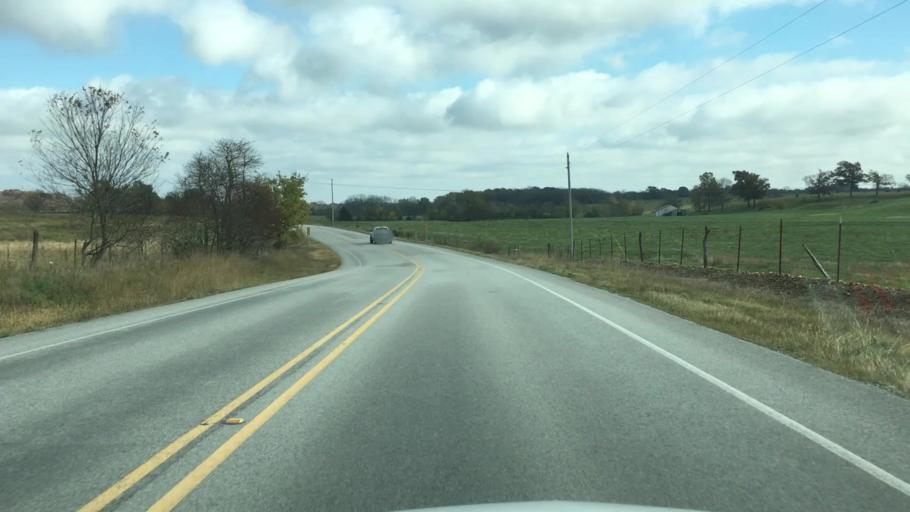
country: US
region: Arkansas
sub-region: Benton County
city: Centerton
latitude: 36.2992
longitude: -94.3371
